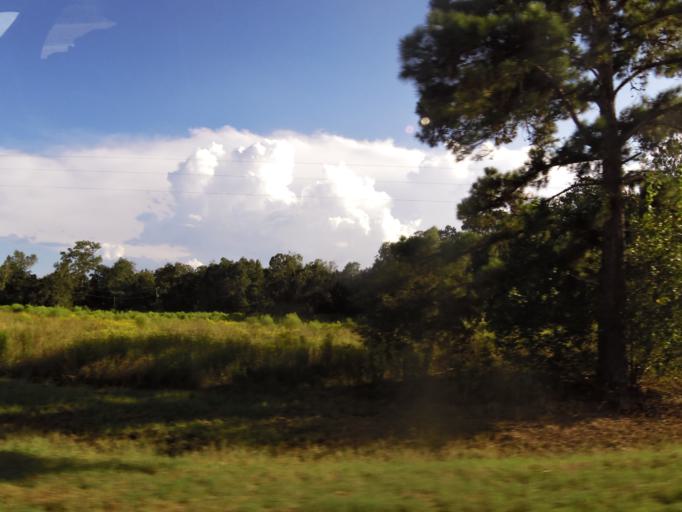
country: US
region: Georgia
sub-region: Brooks County
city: Quitman
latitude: 30.7889
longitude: -83.4977
